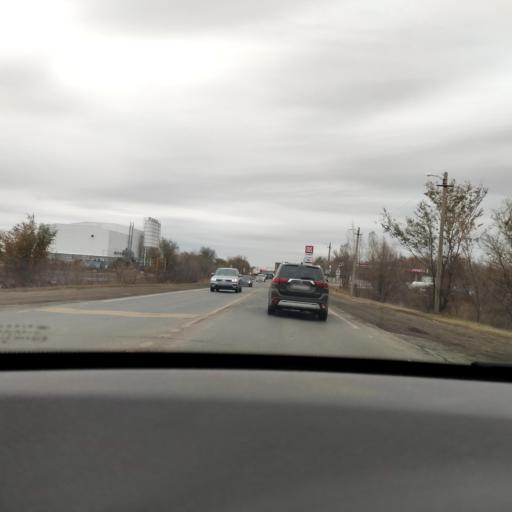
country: RU
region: Samara
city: Samara
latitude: 53.0810
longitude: 50.1111
